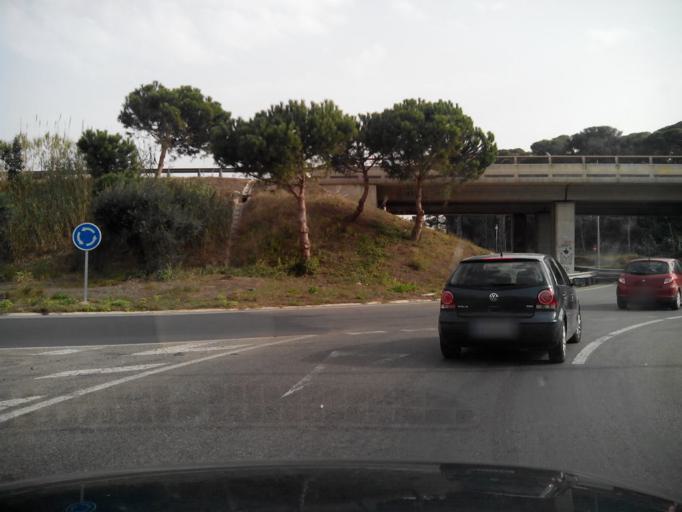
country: ES
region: Catalonia
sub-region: Provincia de Tarragona
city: Reus
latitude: 41.1392
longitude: 1.0982
